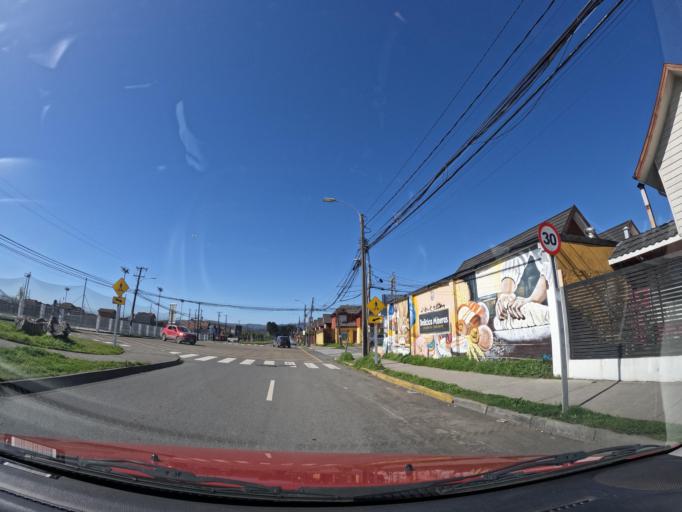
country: CL
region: Biobio
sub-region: Provincia de Concepcion
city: Concepcion
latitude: -36.8823
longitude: -73.1457
